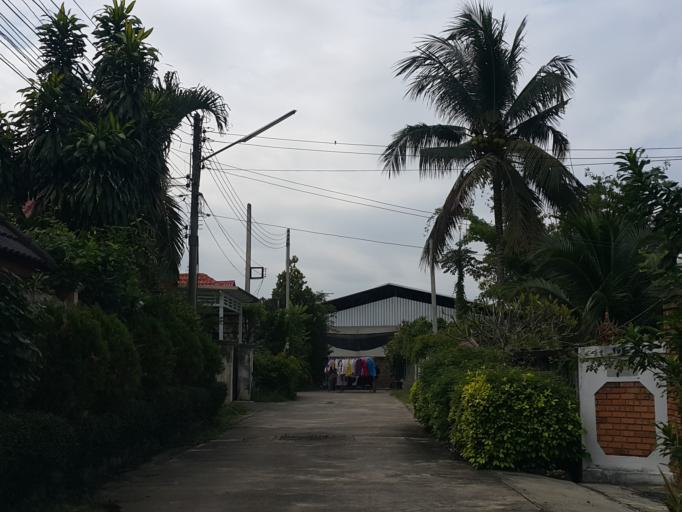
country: TH
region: Lampang
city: Lampang
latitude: 18.3016
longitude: 99.4934
